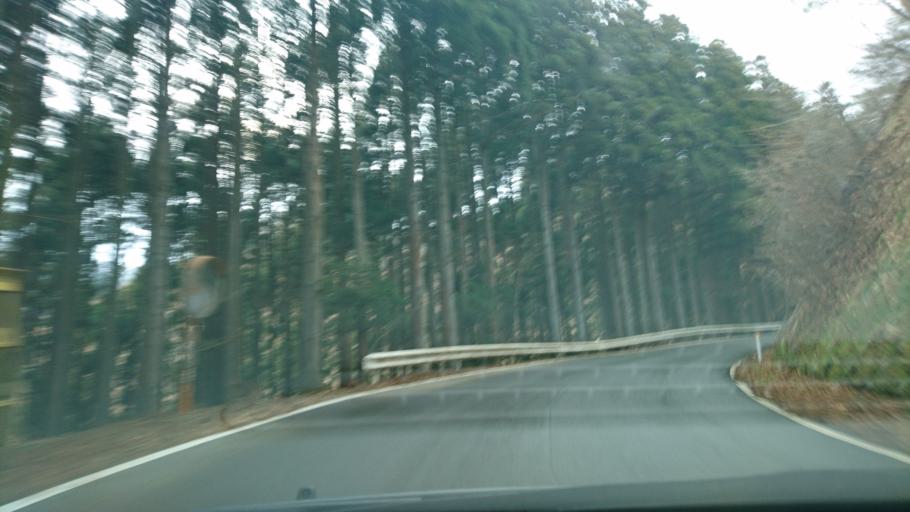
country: JP
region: Iwate
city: Ofunato
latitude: 38.9928
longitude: 141.5487
